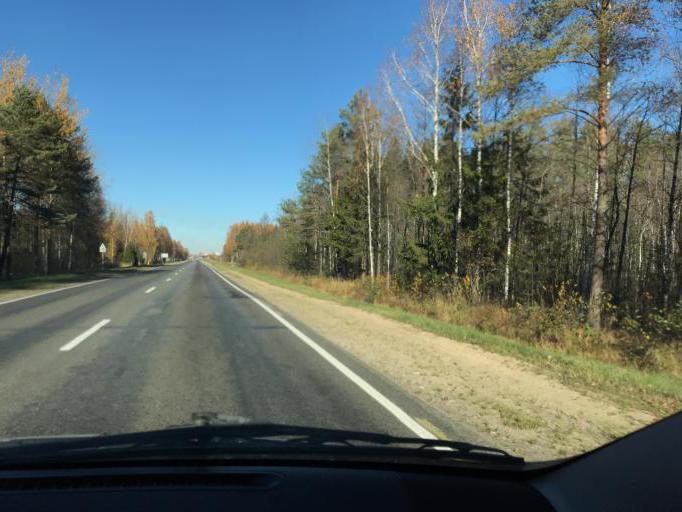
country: BY
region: Vitebsk
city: Polatsk
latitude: 55.4438
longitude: 28.7741
